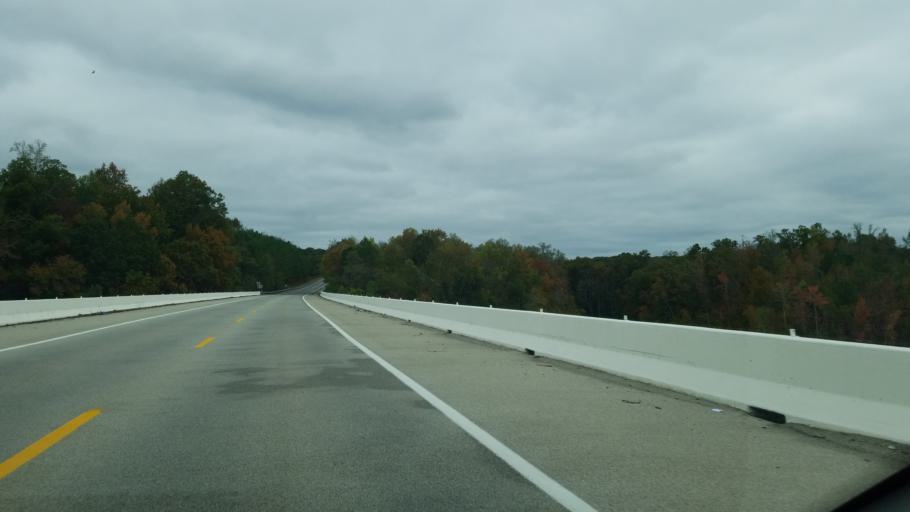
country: US
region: Tennessee
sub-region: Rhea County
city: Graysville
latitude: 35.4129
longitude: -85.0211
